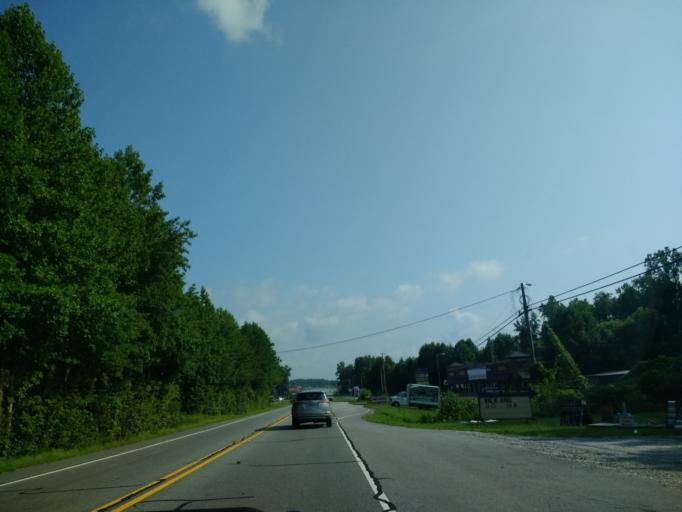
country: US
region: Georgia
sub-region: White County
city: Cleveland
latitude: 34.5663
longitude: -83.7633
